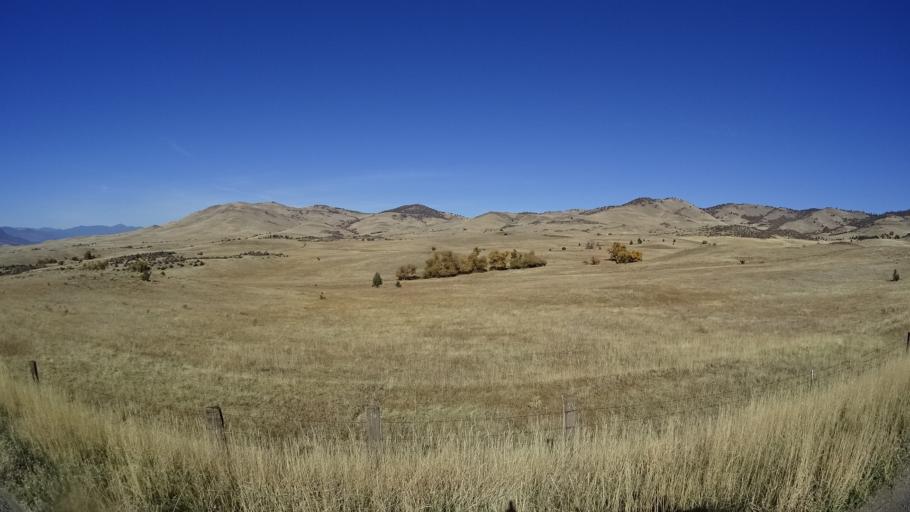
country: US
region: California
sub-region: Siskiyou County
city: Montague
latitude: 41.8133
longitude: -122.3696
